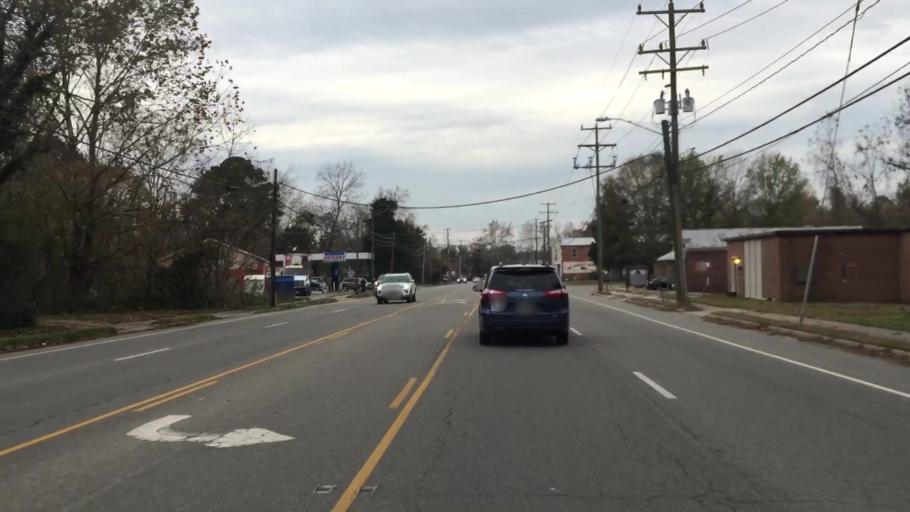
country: US
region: Virginia
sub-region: James City County
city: Williamsburg
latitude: 37.3794
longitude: -76.8031
